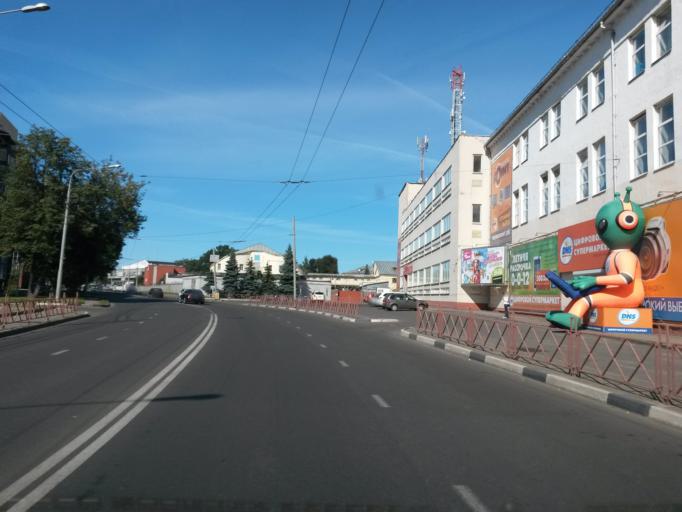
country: RU
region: Jaroslavl
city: Yaroslavl
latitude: 57.6407
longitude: 39.8836
